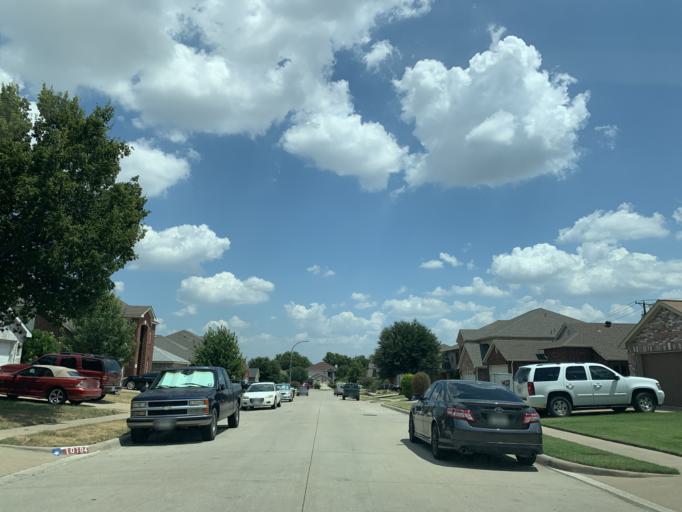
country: US
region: Texas
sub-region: Tarrant County
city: White Settlement
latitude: 32.7264
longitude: -97.5018
